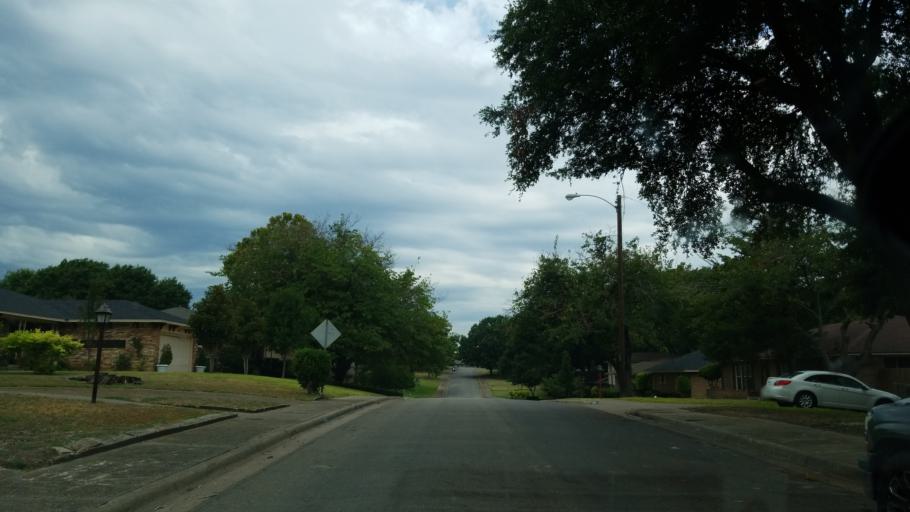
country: US
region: Texas
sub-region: Dallas County
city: Duncanville
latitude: 32.6660
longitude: -96.8371
